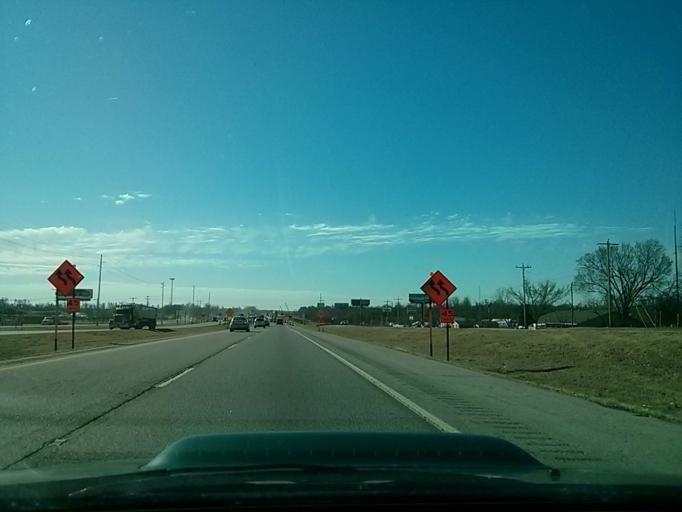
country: US
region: Oklahoma
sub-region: Tulsa County
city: Owasso
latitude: 36.2526
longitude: -95.8482
